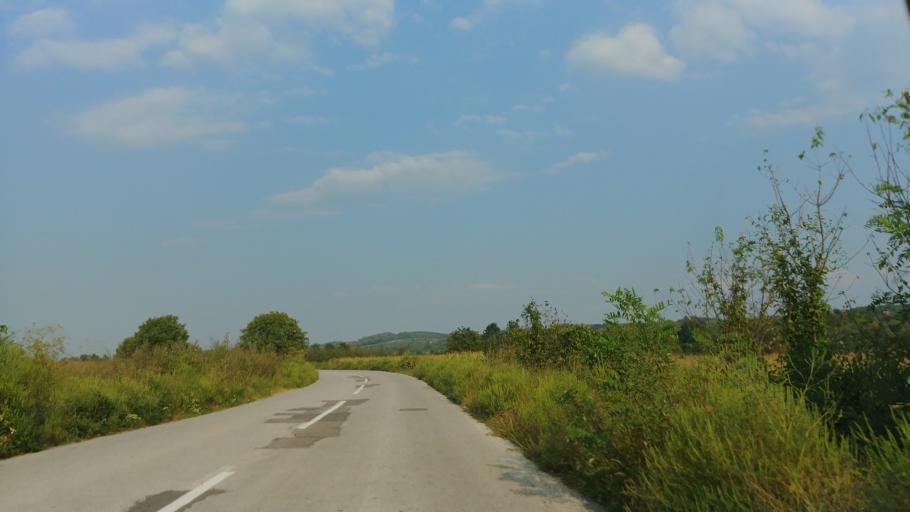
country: BA
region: Republika Srpska
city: Lopare
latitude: 44.7324
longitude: 18.8445
